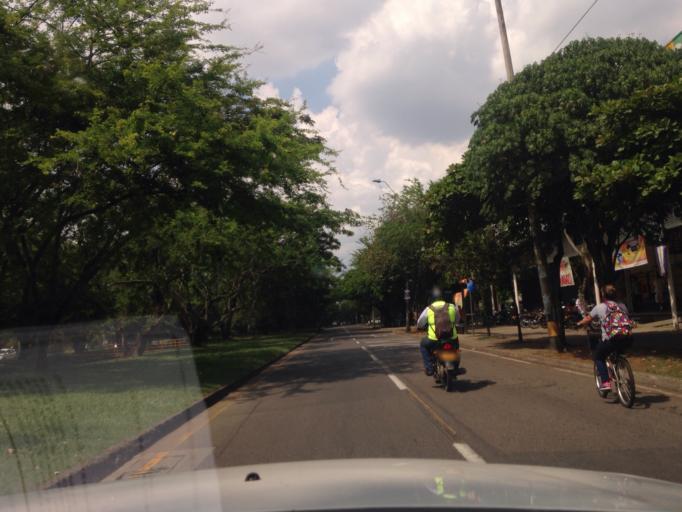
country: CO
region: Valle del Cauca
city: Cali
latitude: 3.3823
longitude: -76.5162
